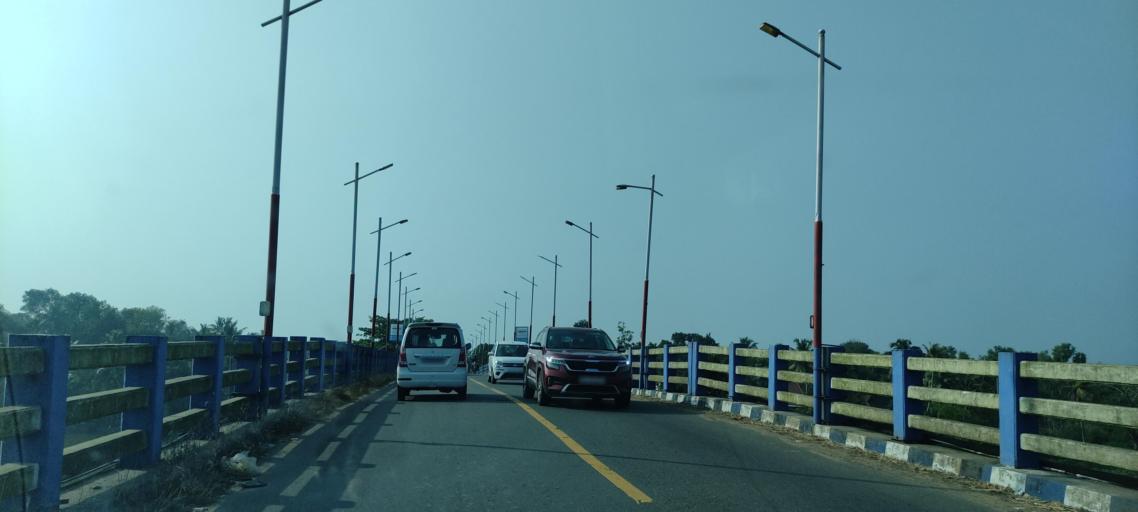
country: IN
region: Kerala
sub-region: Kottayam
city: Changanacheri
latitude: 9.3703
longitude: 76.4249
